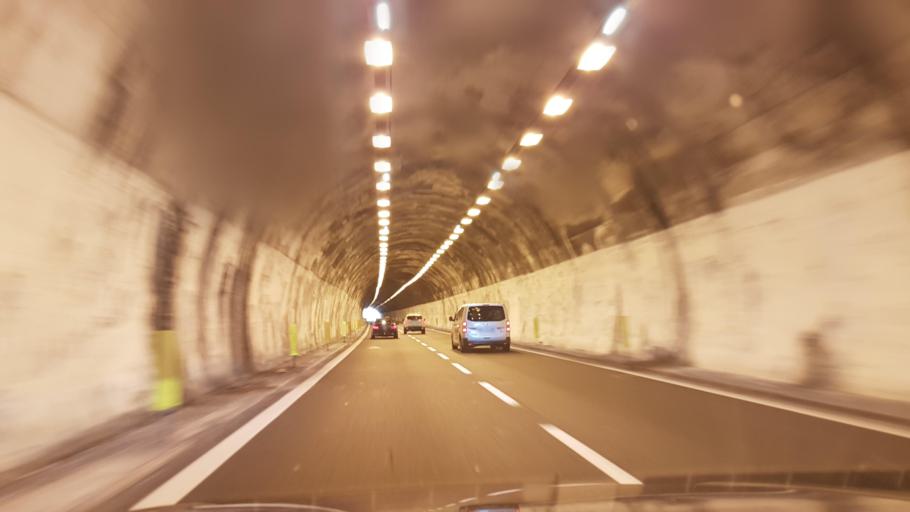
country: IT
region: Liguria
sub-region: Provincia di Savona
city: Loano
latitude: 44.1505
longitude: 8.2579
